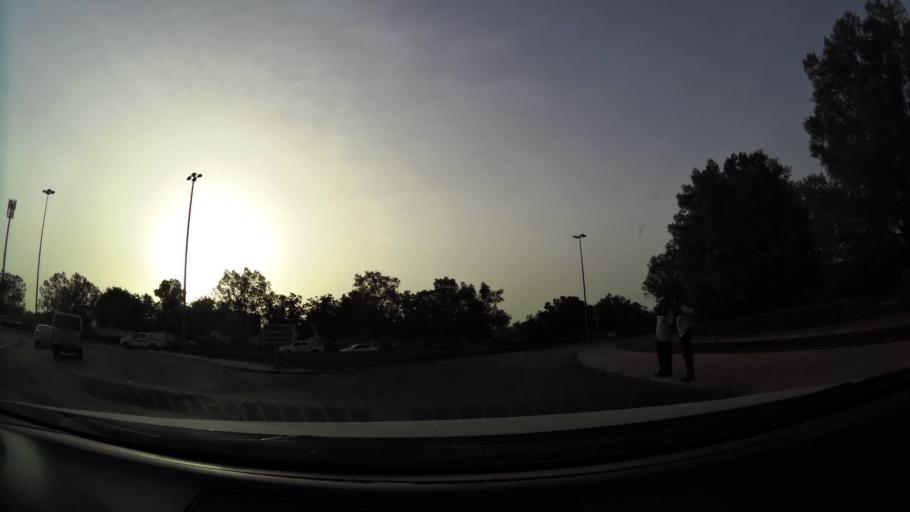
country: AE
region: Abu Dhabi
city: Al Ain
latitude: 24.2487
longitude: 55.7199
